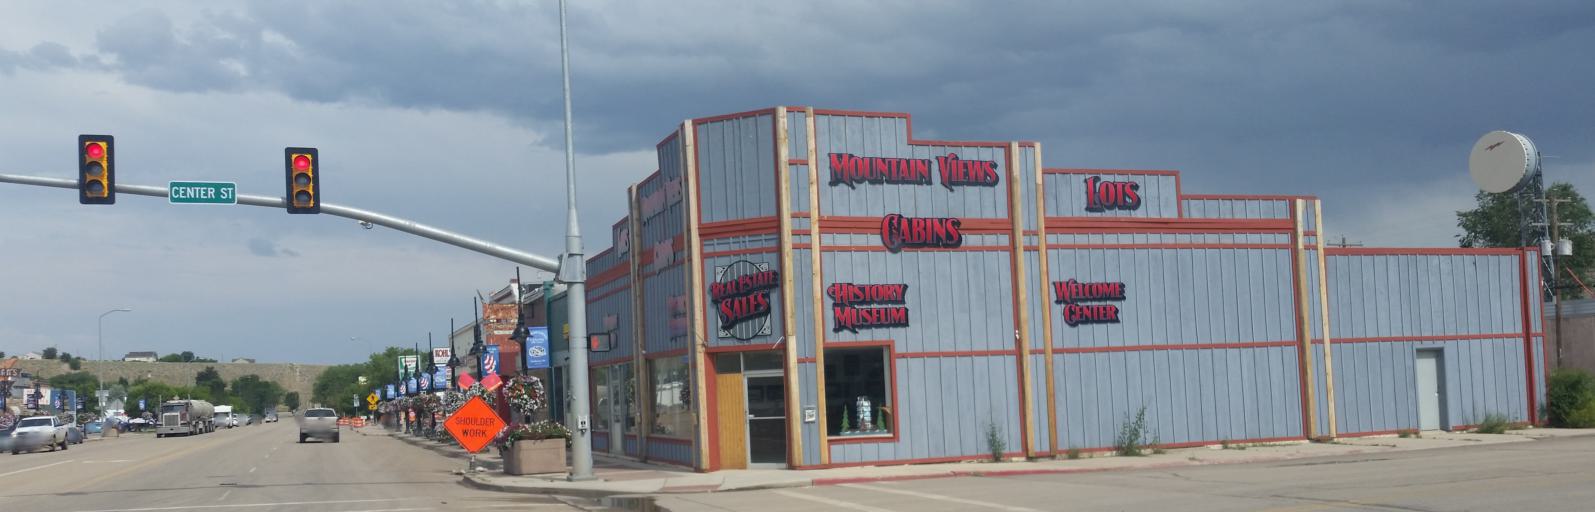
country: US
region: Utah
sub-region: Duchesne County
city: Duchesne
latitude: 40.1634
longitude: -110.4019
